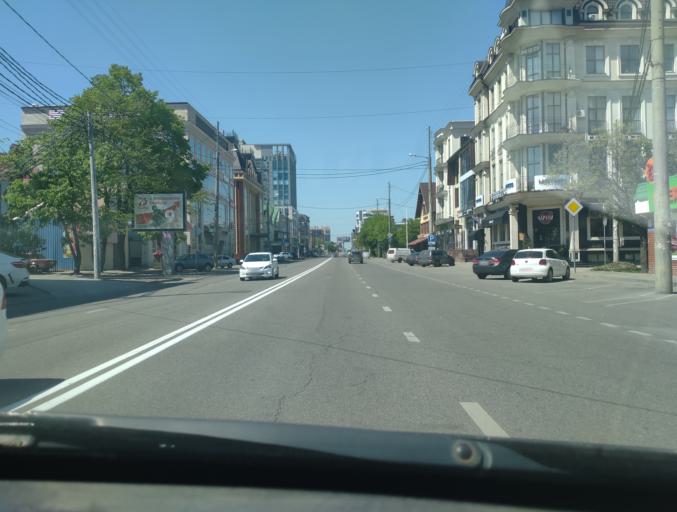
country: RU
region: Krasnodarskiy
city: Krasnodar
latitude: 45.0496
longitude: 38.9675
